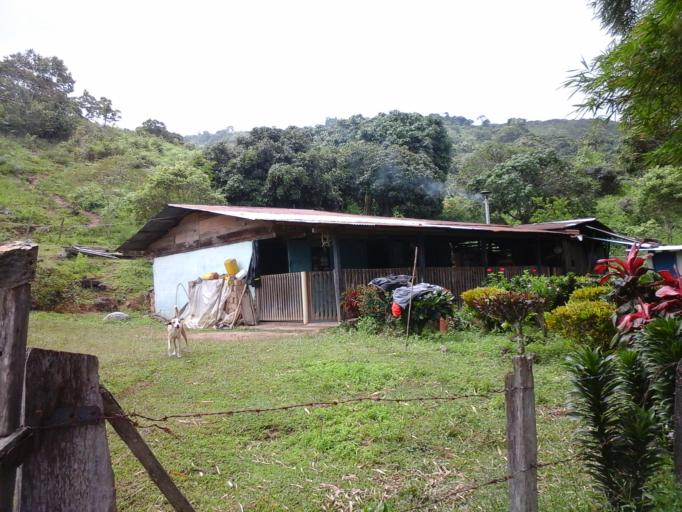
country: CO
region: Cesar
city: Agustin Codazzi
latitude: 9.9554
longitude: -73.0634
